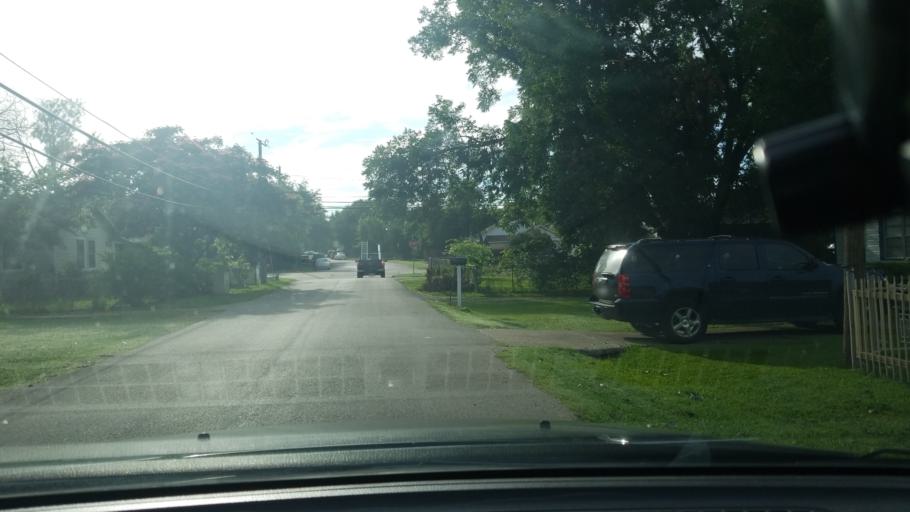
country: US
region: Texas
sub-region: Dallas County
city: Balch Springs
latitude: 32.7570
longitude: -96.6489
